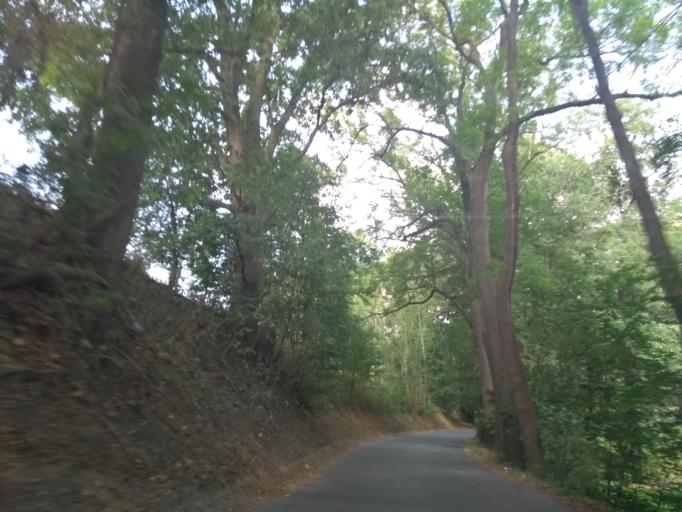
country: DE
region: Thuringia
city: Walpernhain
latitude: 50.9991
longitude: 11.9780
